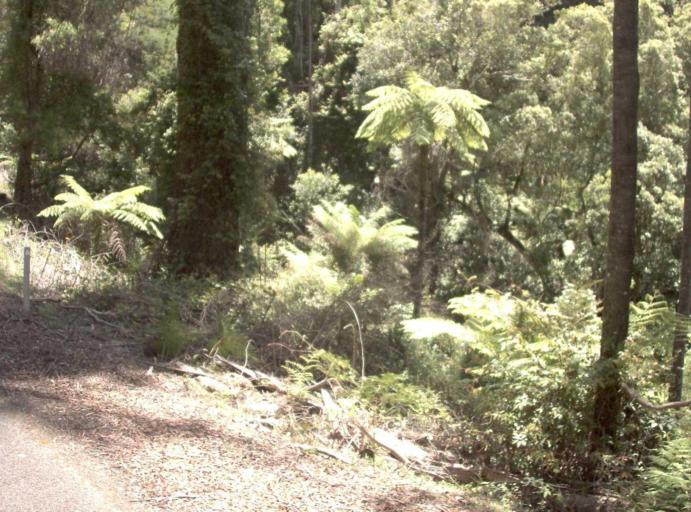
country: AU
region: New South Wales
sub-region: Bombala
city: Bombala
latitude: -37.4556
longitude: 148.9324
